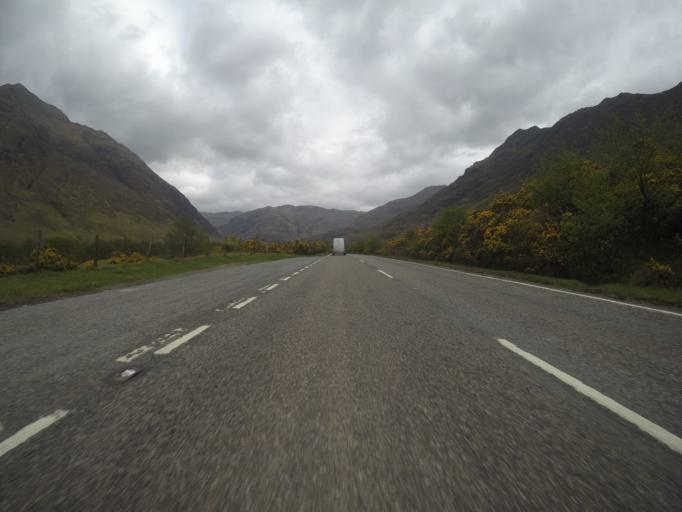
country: GB
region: Scotland
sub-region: Highland
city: Fort William
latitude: 57.1911
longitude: -5.3862
